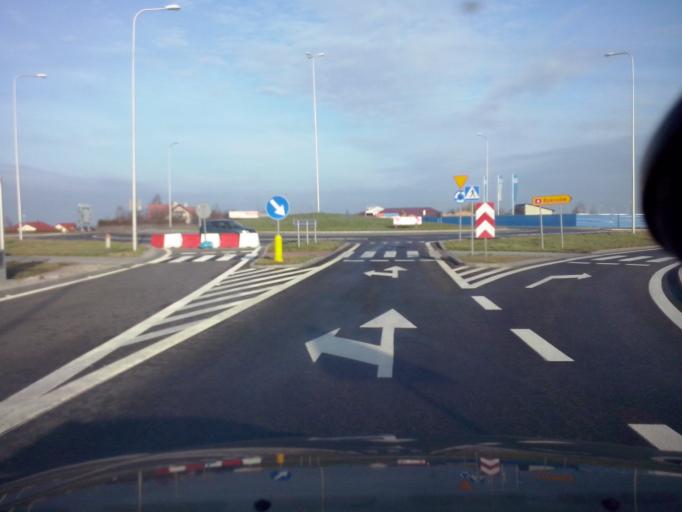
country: PL
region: Subcarpathian Voivodeship
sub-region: Rzeszow
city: Przybyszowka
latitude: 50.0654
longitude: 21.9252
